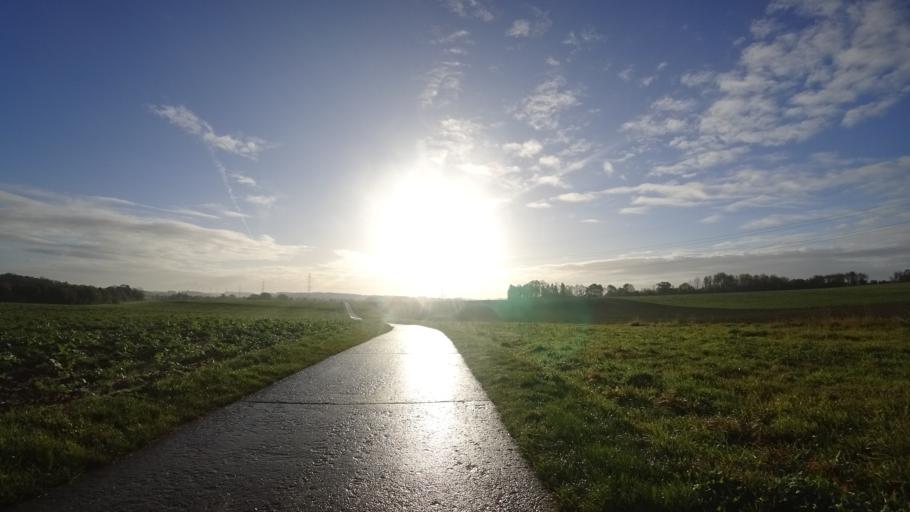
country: BE
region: Wallonia
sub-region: Province de Namur
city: Floreffe
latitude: 50.5124
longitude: 4.7897
